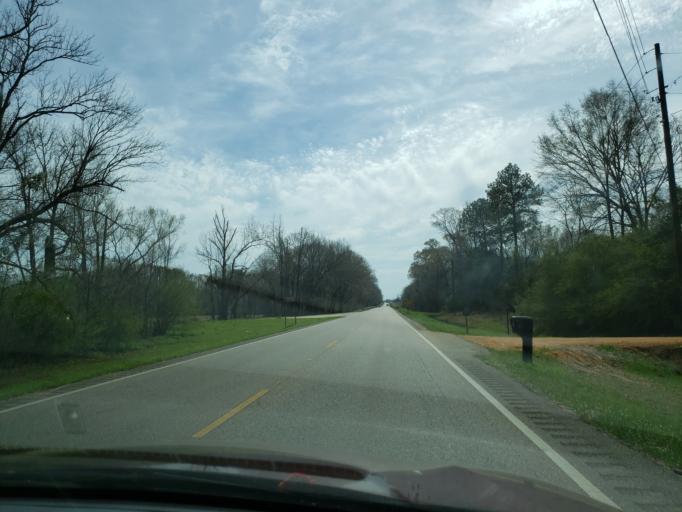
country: US
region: Alabama
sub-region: Dallas County
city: Selma
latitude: 32.4523
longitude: -87.0796
